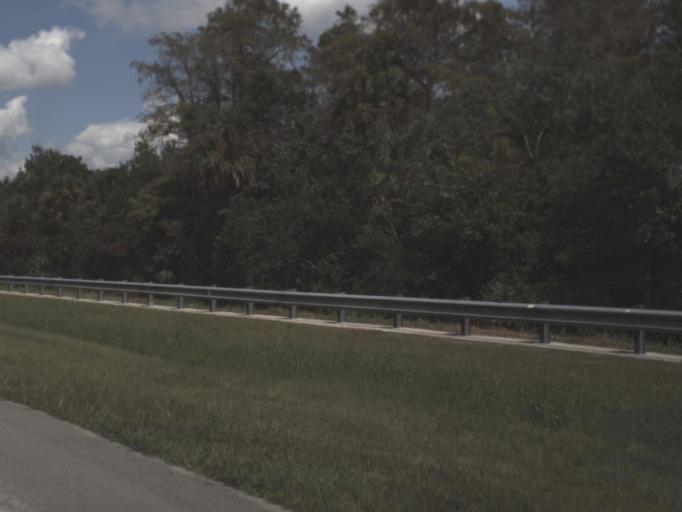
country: US
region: Florida
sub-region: Collier County
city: Orangetree
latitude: 26.0827
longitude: -81.3447
